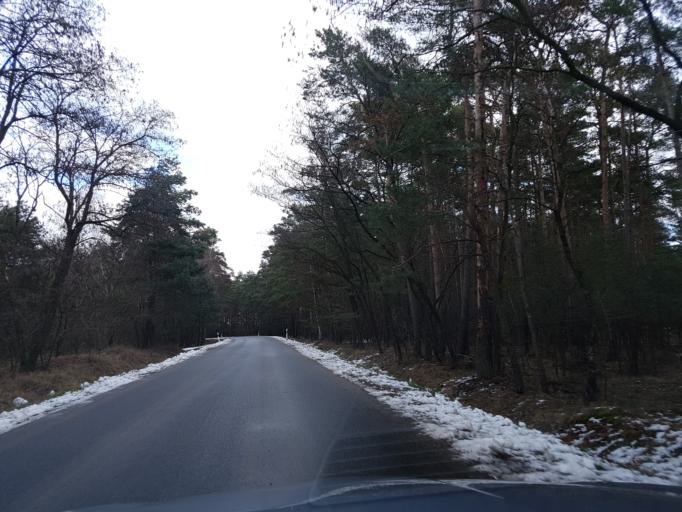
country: DE
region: Brandenburg
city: Merzdorf
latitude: 51.3960
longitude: 13.5253
